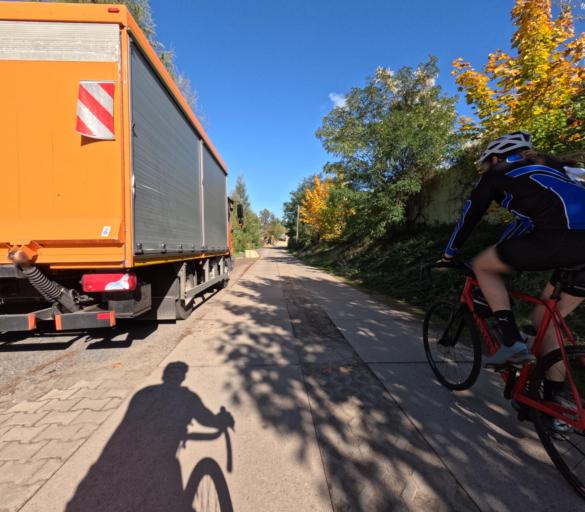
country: DE
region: Saxony
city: Albertstadt
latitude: 51.0880
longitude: 13.7600
